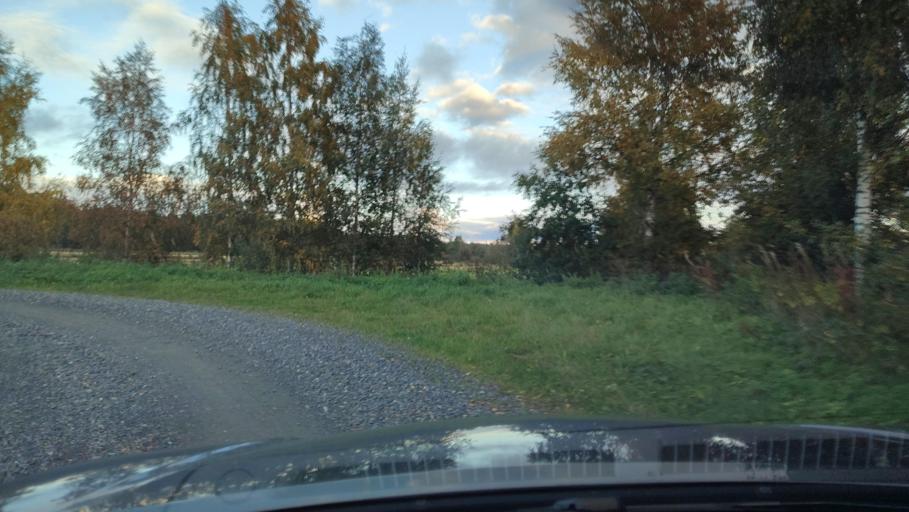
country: FI
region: Ostrobothnia
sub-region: Sydosterbotten
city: Kristinestad
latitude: 62.2388
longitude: 21.4555
